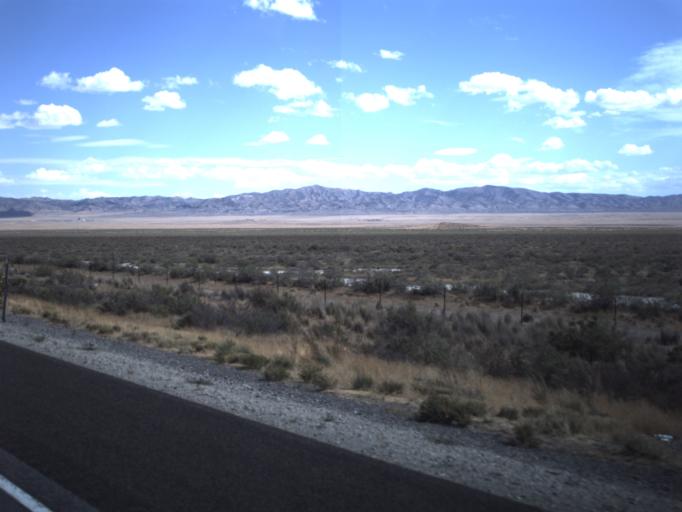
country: US
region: Utah
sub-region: Tooele County
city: Grantsville
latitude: 40.7365
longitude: -113.0957
